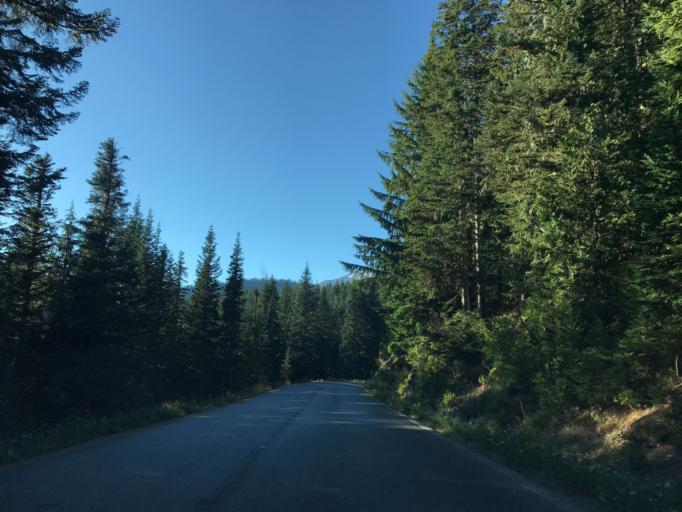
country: US
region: Washington
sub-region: Pierce County
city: Buckley
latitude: 46.7748
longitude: -121.7523
